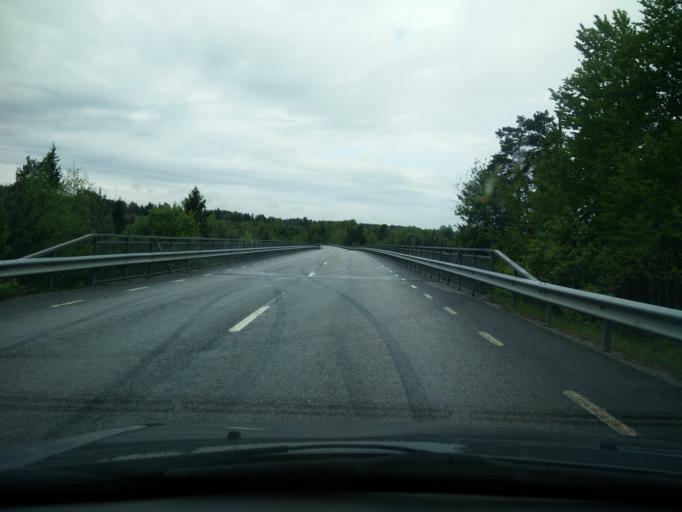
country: SE
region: Stockholm
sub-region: Norrtalje Kommun
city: Bjorko
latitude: 59.8185
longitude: 18.9193
